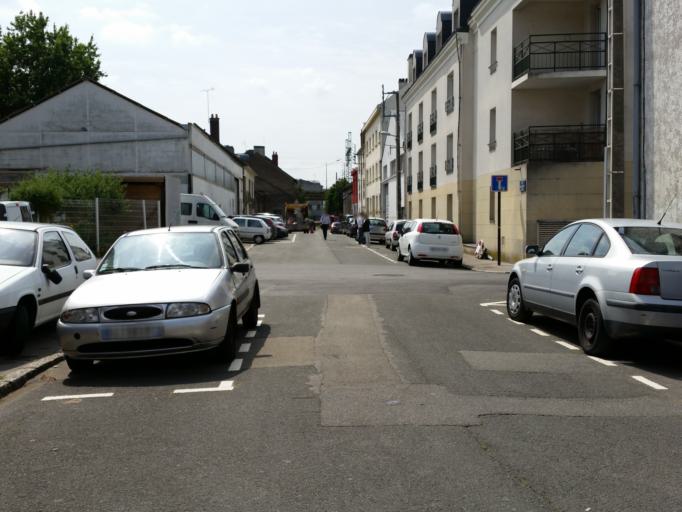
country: FR
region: Pays de la Loire
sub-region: Departement de la Loire-Atlantique
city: Nantes
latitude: 47.2032
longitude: -1.5484
